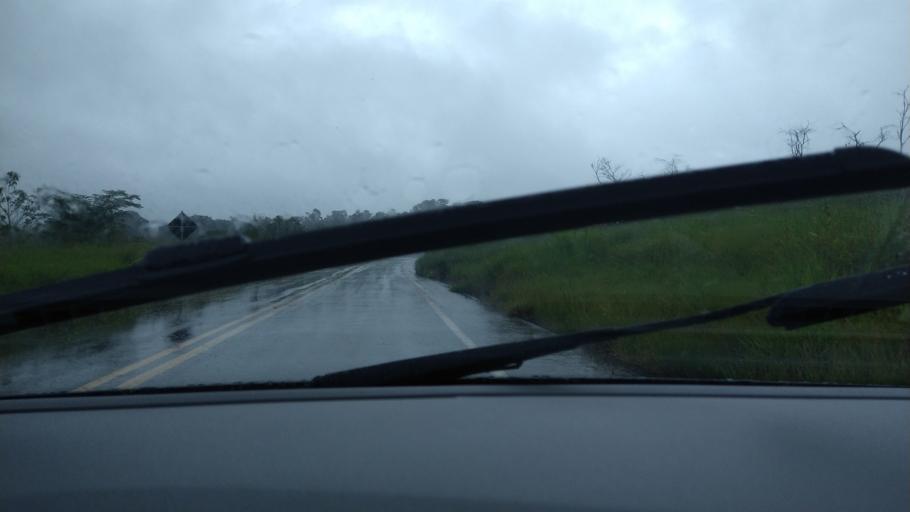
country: BR
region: Minas Gerais
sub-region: Ponte Nova
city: Ponte Nova
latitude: -20.5534
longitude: -42.8746
